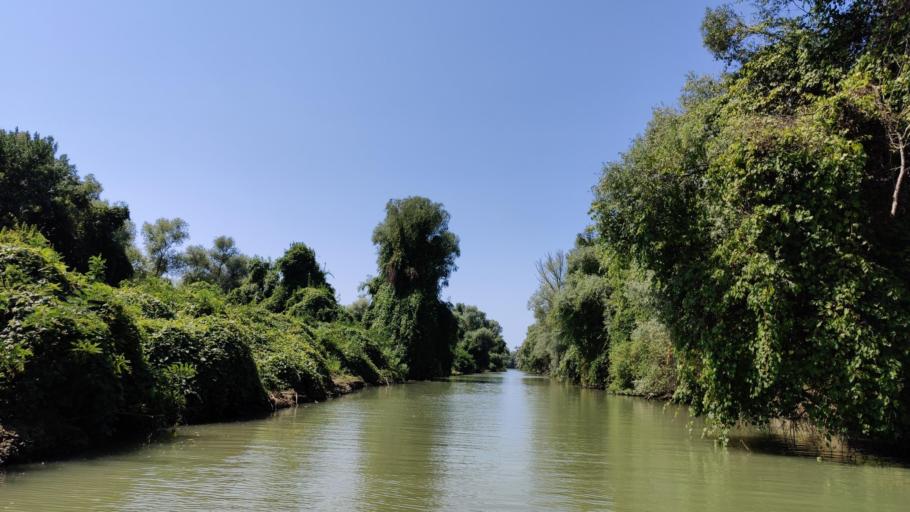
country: RO
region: Tulcea
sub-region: Comuna Pardina
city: Pardina
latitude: 45.2546
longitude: 28.9365
